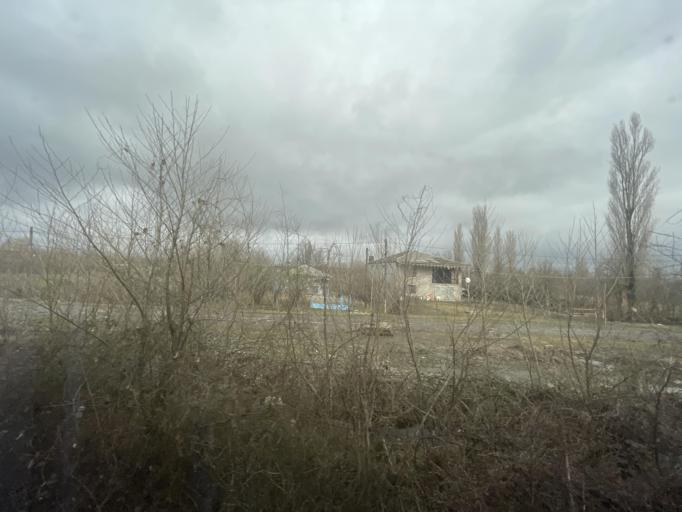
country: GE
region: Guria
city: Lanchkhuti
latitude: 42.0960
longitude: 42.0252
